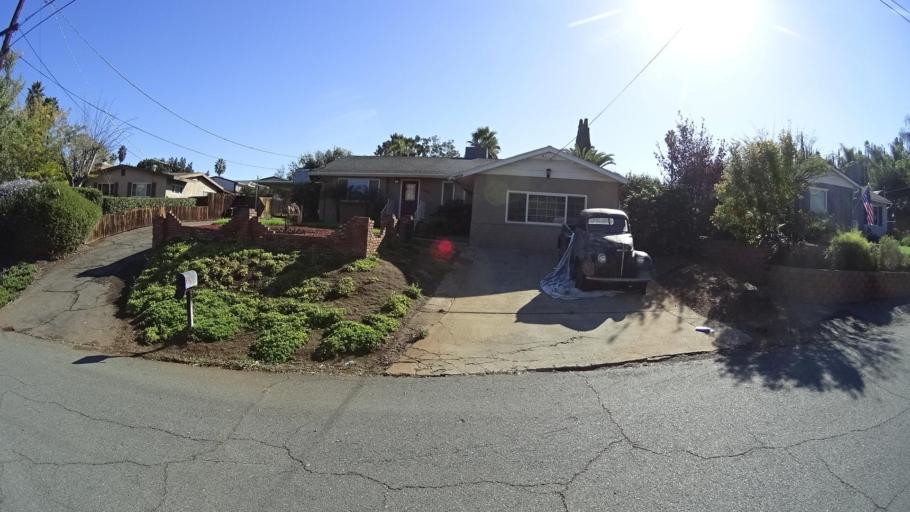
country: US
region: California
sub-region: San Diego County
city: Bostonia
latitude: 32.8189
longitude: -116.9342
